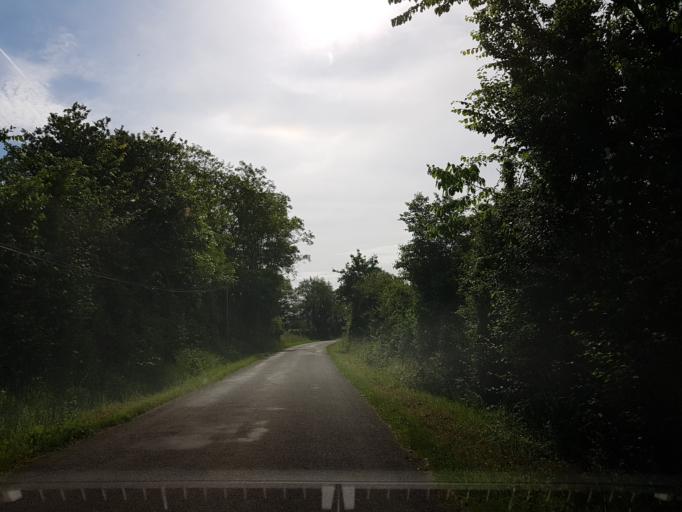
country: FR
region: Poitou-Charentes
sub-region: Departement de la Charente
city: Etagnac
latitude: 45.9338
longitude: 0.7335
